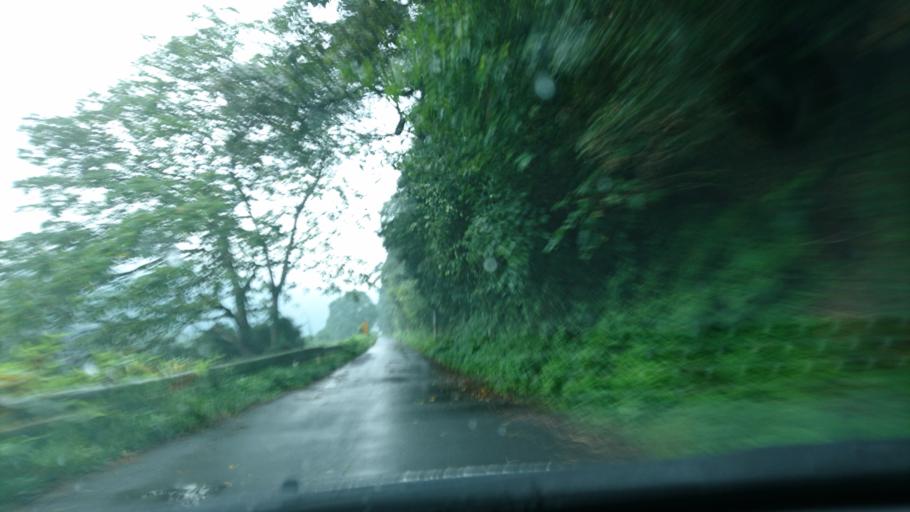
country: JP
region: Iwate
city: Ichinoseki
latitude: 38.8757
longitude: 141.2594
